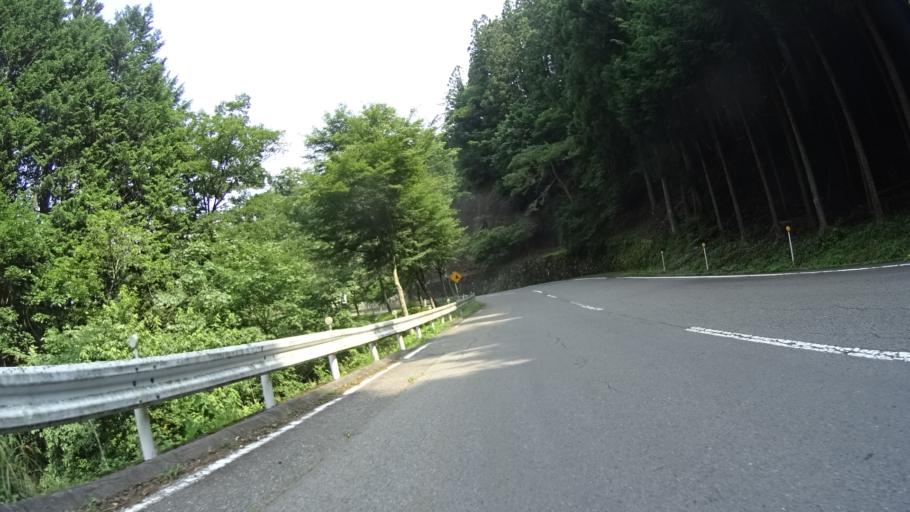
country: JP
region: Gunma
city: Tomioka
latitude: 36.0595
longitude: 138.8426
